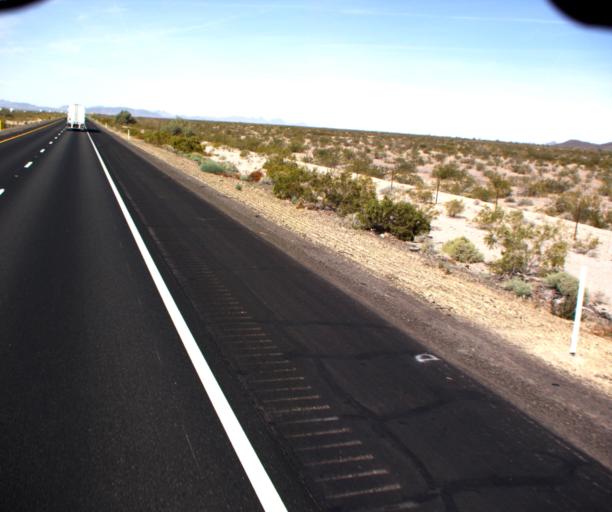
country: US
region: Arizona
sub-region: La Paz County
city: Salome
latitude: 33.6157
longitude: -113.6622
